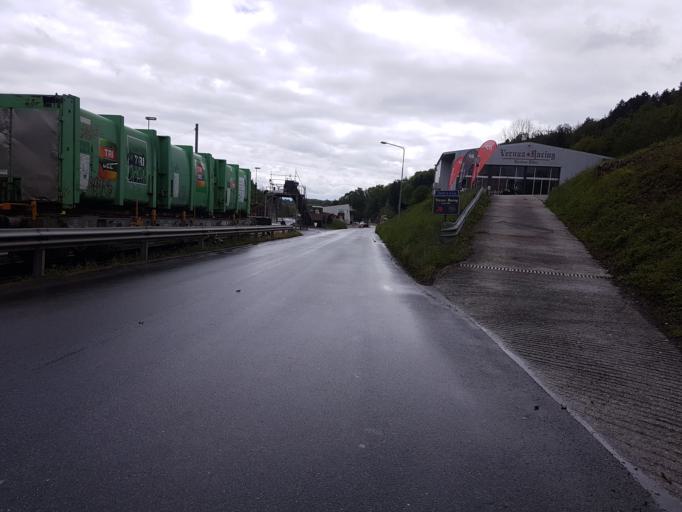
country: CH
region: Vaud
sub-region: Gros-de-Vaud District
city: Penthalaz
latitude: 46.6031
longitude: 6.5242
